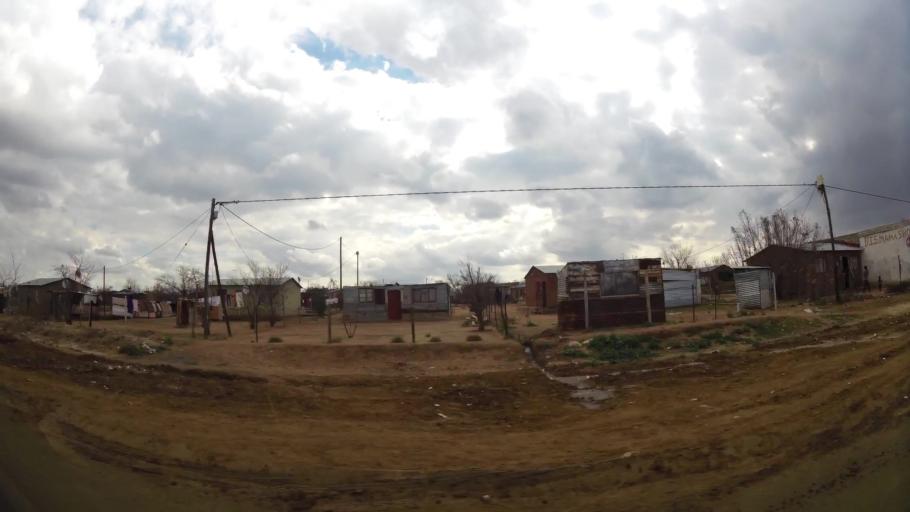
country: ZA
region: Orange Free State
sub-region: Fezile Dabi District Municipality
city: Sasolburg
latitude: -26.8707
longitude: 27.8739
